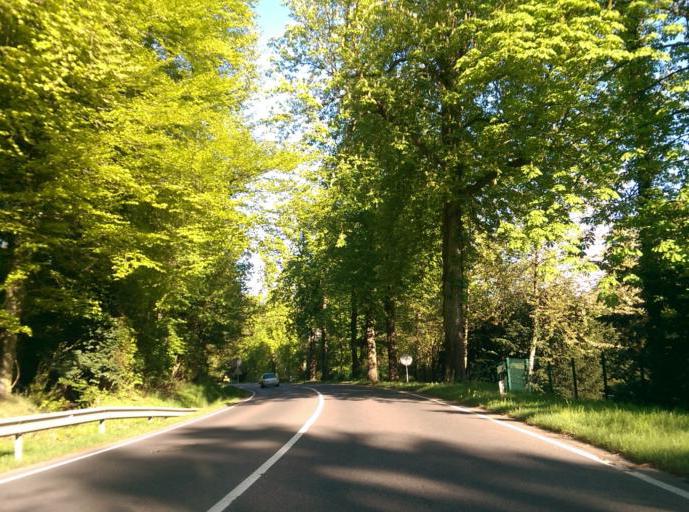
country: LU
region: Luxembourg
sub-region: Canton de Luxembourg
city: Niederanven
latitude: 49.6477
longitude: 6.2346
